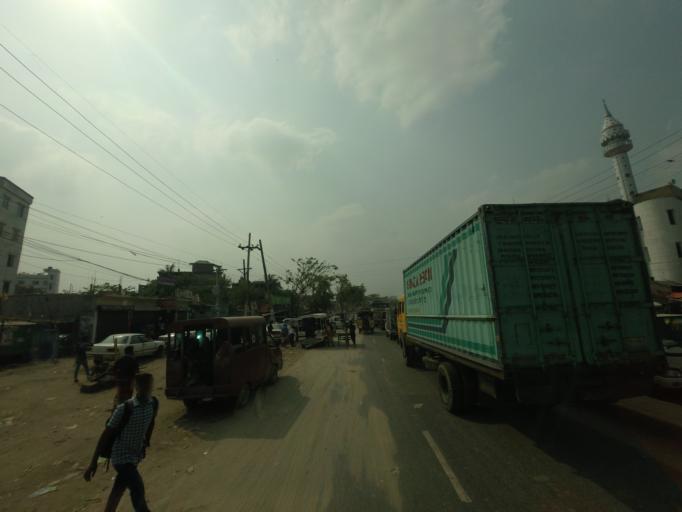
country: BD
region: Dhaka
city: Azimpur
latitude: 23.7863
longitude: 90.3295
